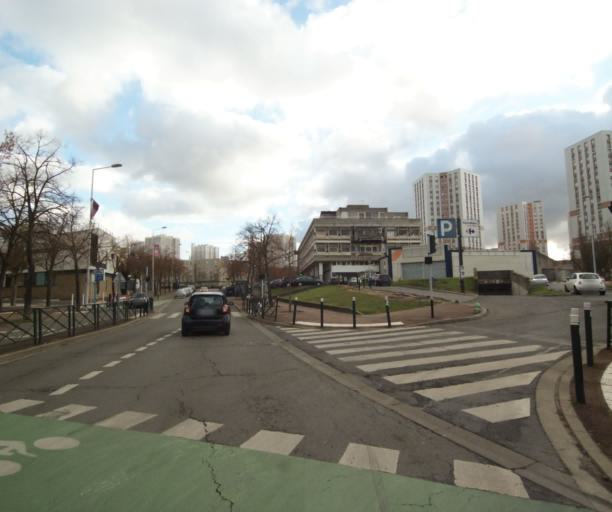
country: FR
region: Ile-de-France
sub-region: Departement des Hauts-de-Seine
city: Nanterre
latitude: 48.8899
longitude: 2.2194
